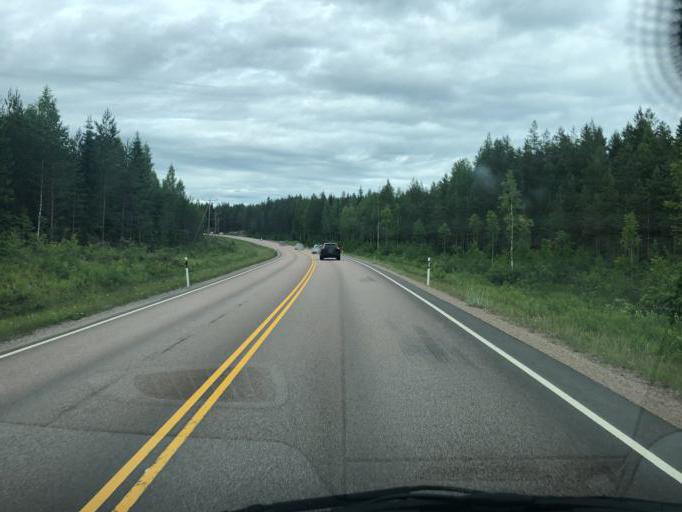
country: FI
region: Southern Savonia
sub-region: Mikkeli
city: Ristiina
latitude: 61.1638
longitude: 27.1464
